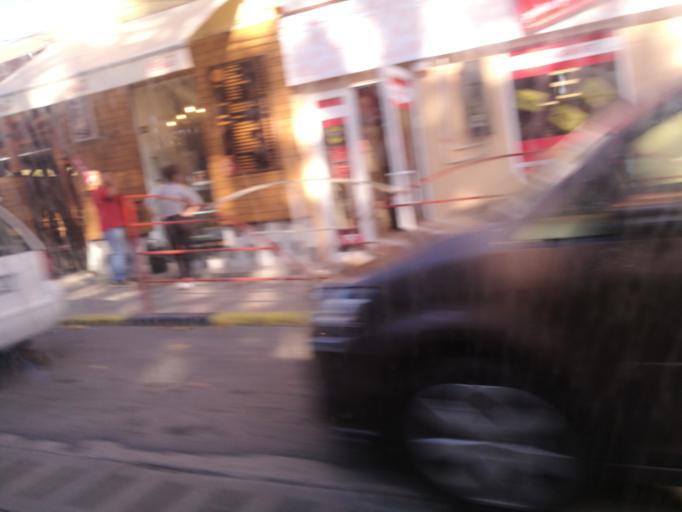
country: RO
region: Prahova
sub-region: Comuna Comarnic
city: Ghiosesti
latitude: 45.2430
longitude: 25.6332
